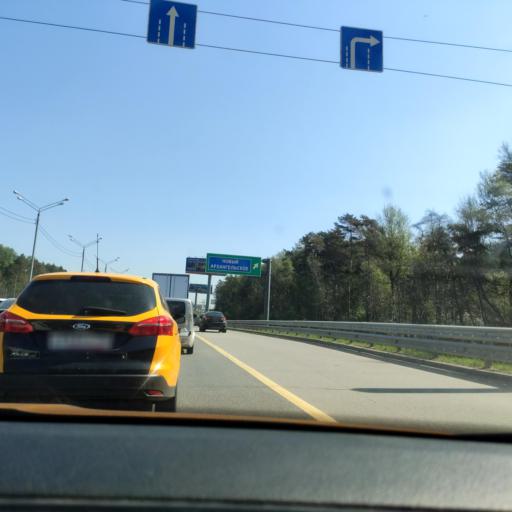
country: RU
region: Moskovskaya
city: Arkhangel'skoye
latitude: 55.7994
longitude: 37.2837
